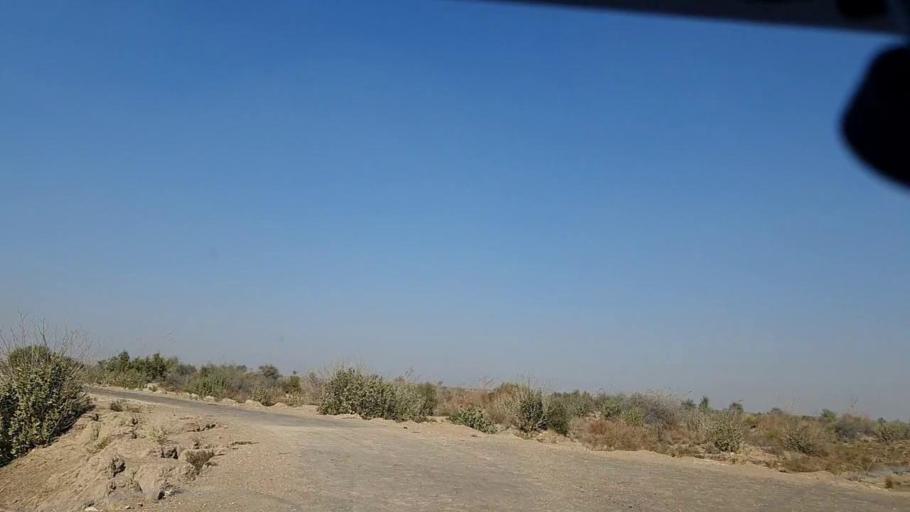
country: PK
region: Sindh
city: Khanpur
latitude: 27.5759
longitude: 69.3798
